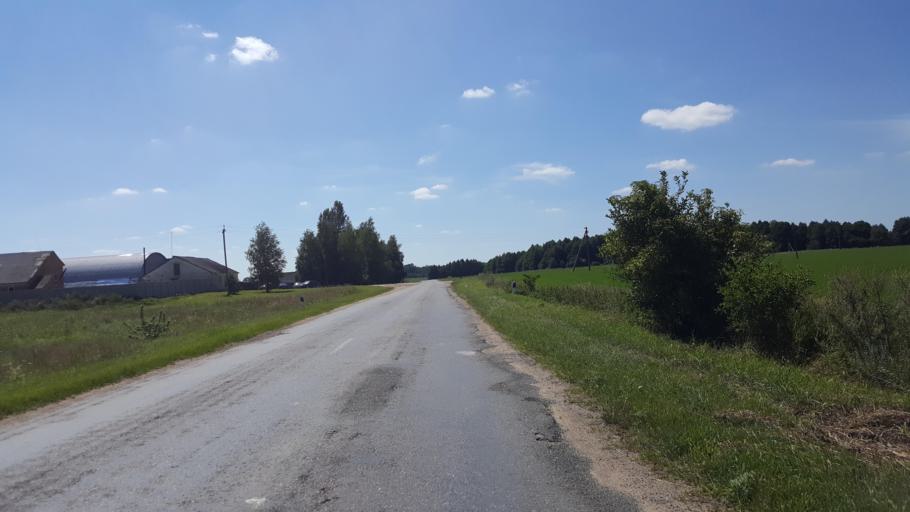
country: BY
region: Brest
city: Charnawchytsy
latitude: 52.3408
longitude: 23.6055
